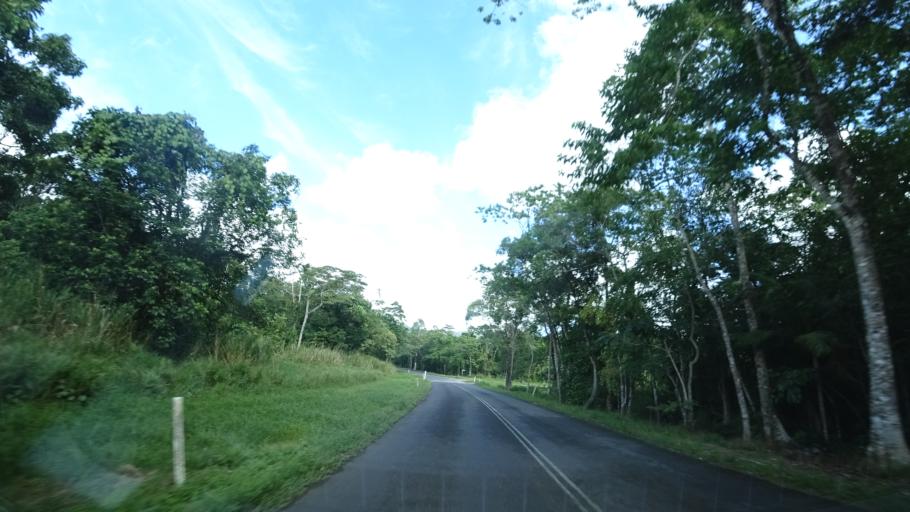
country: AU
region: Queensland
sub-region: Cairns
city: Port Douglas
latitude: -16.2080
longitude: 145.4054
